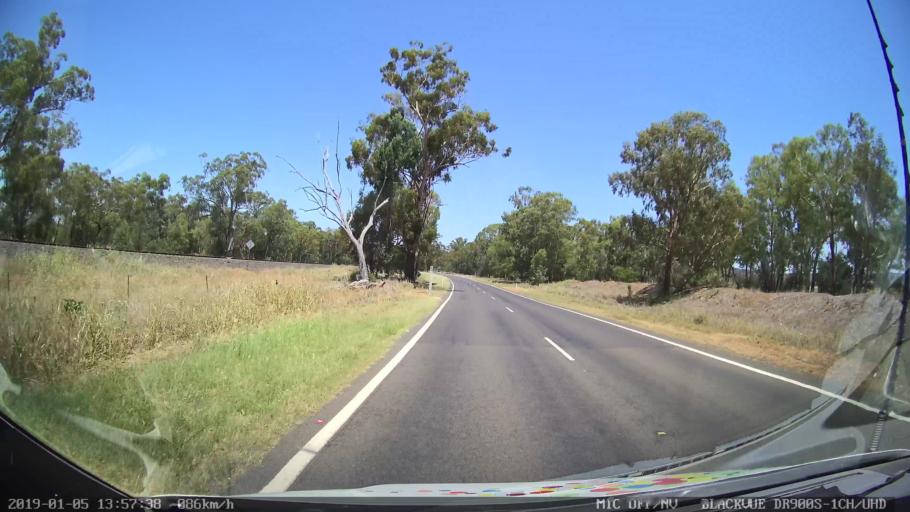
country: AU
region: New South Wales
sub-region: Gunnedah
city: Gunnedah
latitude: -31.1298
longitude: 150.2757
